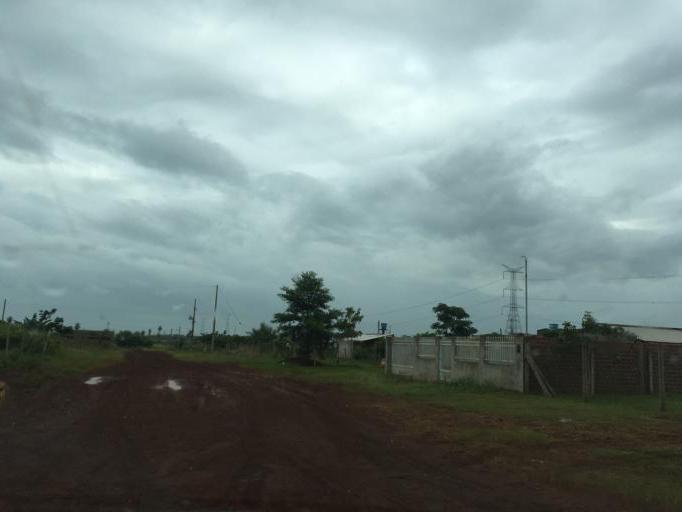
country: PY
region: Alto Parana
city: Ciudad del Este
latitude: -25.4291
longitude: -54.6512
